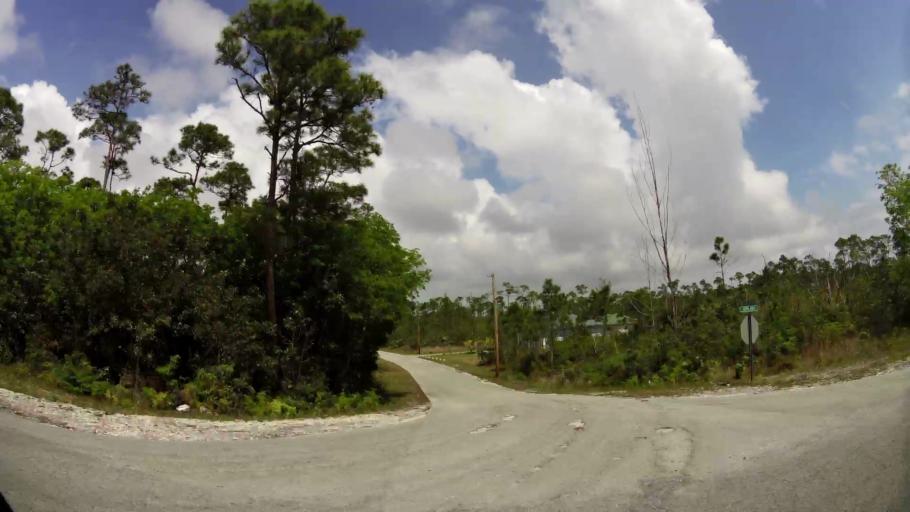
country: BS
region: Freeport
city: Lucaya
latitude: 26.5331
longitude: -78.6293
